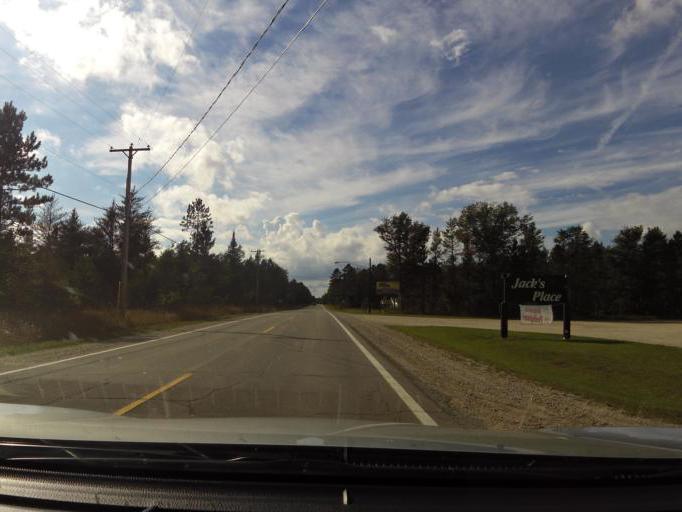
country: US
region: Michigan
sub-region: Roscommon County
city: Roscommon
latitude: 44.5110
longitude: -84.5618
